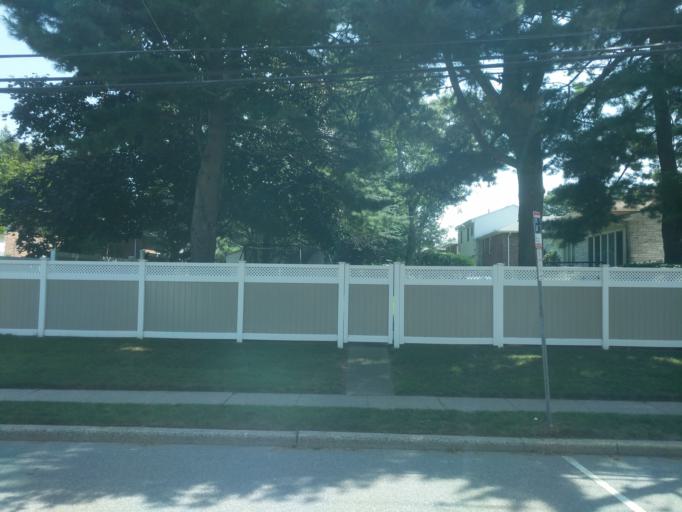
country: US
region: New York
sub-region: Nassau County
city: Lakeview
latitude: 40.6903
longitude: -73.6584
